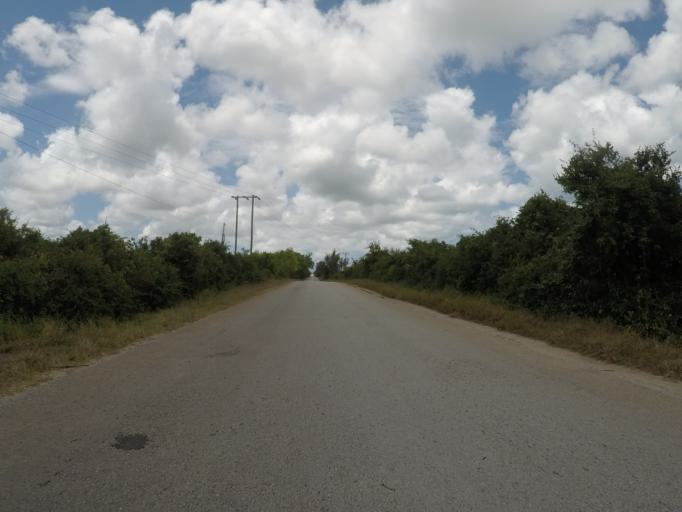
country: TZ
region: Zanzibar Central/South
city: Mahonda
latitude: -6.3165
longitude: 39.4328
